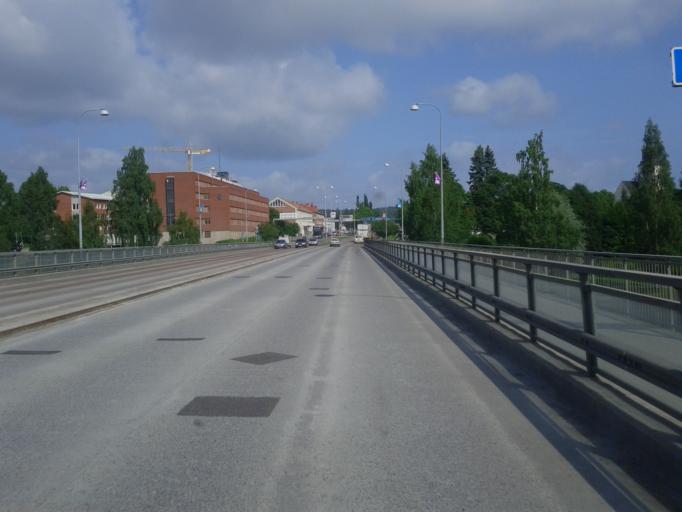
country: SE
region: Vaesterbotten
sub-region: Skelleftea Kommun
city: Skelleftea
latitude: 64.7471
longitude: 20.9600
